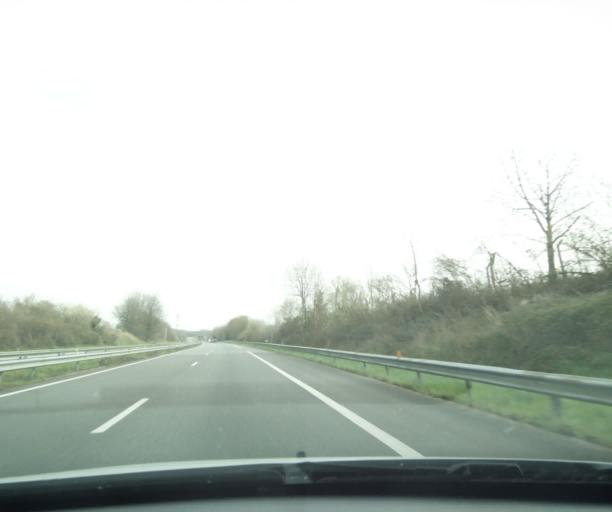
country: FR
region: Aquitaine
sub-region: Departement des Pyrenees-Atlantiques
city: Orthez
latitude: 43.4797
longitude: -0.8036
